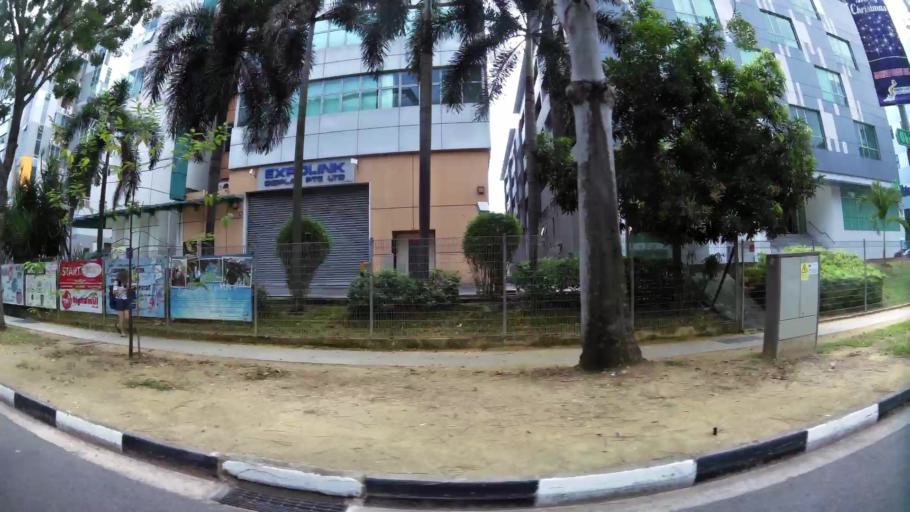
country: SG
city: Singapore
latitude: 1.3251
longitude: 103.8945
